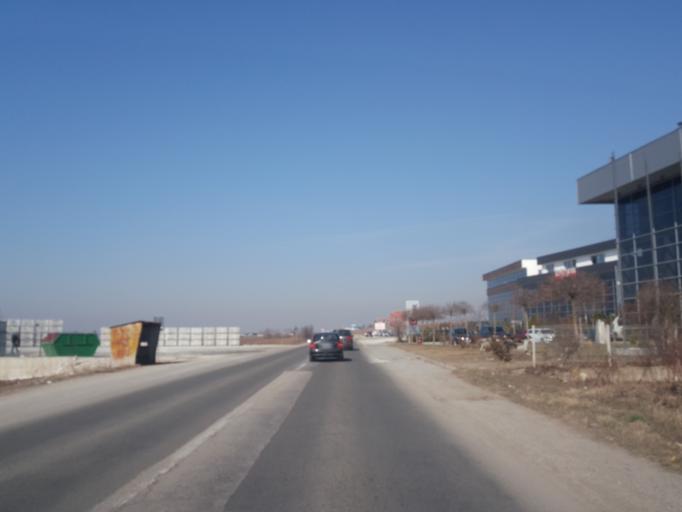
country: XK
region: Mitrovica
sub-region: Vushtrri
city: Vushtrri
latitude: 42.7687
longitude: 21.0227
